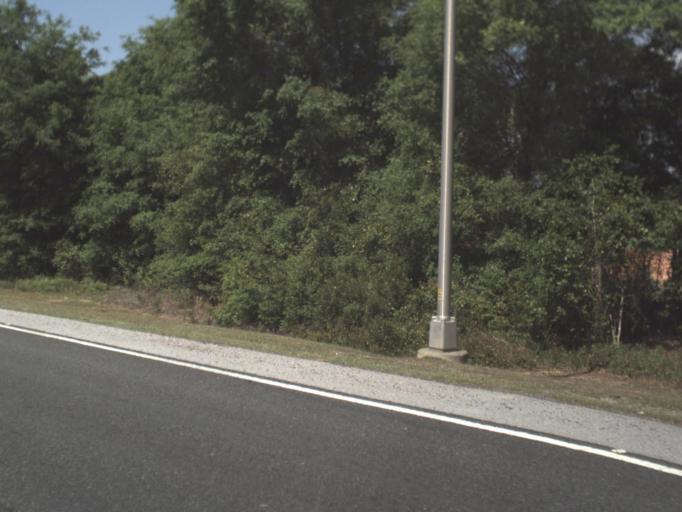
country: US
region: Florida
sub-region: Santa Rosa County
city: East Milton
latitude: 30.6083
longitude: -86.9818
